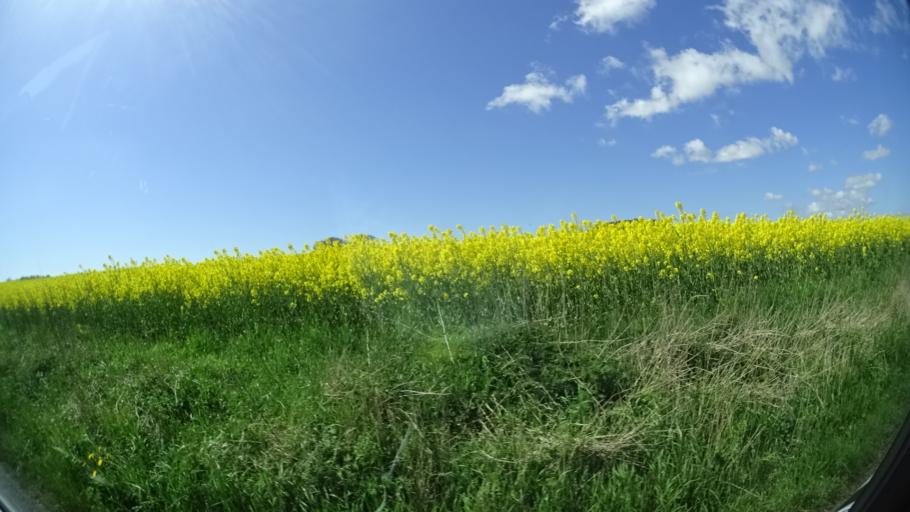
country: DK
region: Central Jutland
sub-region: Skanderborg Kommune
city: Horning
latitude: 56.1107
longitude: 10.0265
